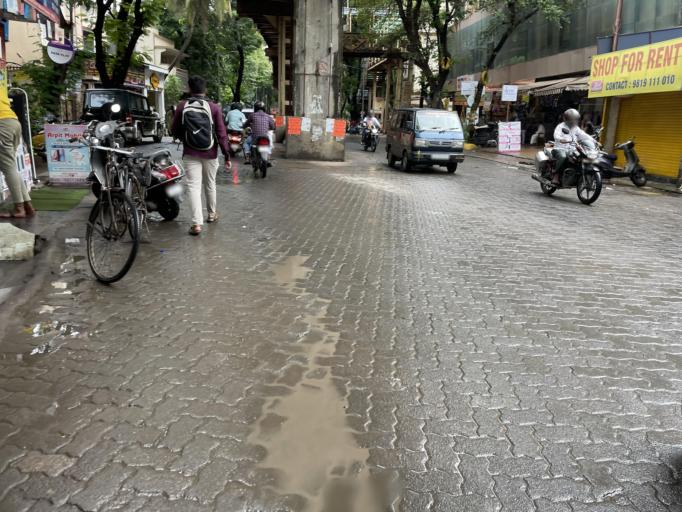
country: IN
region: Maharashtra
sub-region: Mumbai Suburban
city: Borivli
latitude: 19.2533
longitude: 72.8584
